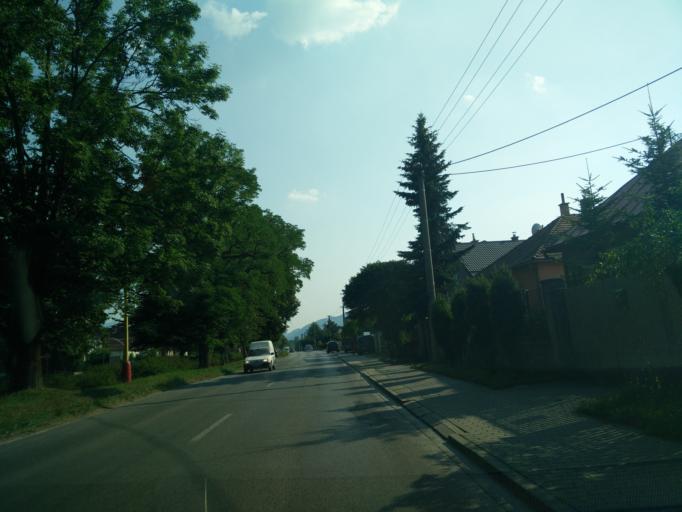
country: SK
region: Zilinsky
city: Rajec
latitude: 49.0837
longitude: 18.6334
